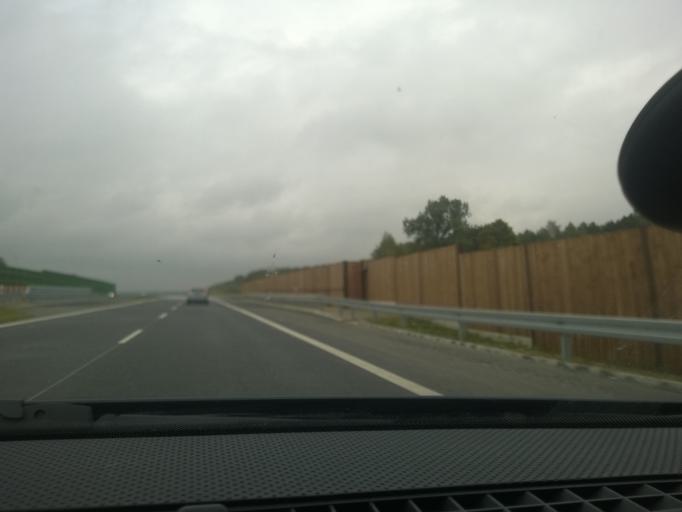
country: PL
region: Lodz Voivodeship
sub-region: Powiat zgierski
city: Strykow
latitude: 51.8264
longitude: 19.6515
